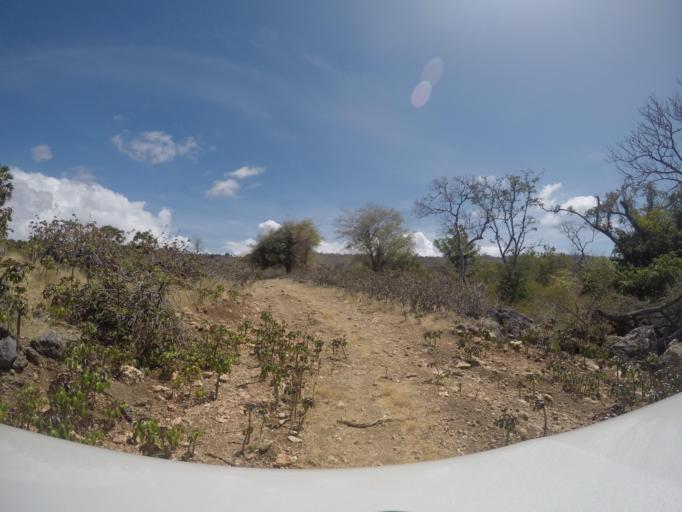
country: TL
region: Baucau
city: Baucau
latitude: -8.4334
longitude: 126.4409
